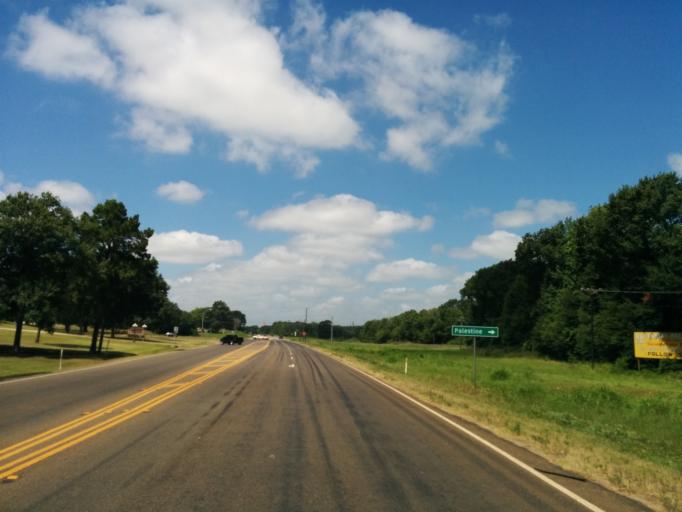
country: US
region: Texas
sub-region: Houston County
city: Crockett
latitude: 31.3370
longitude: -95.4642
